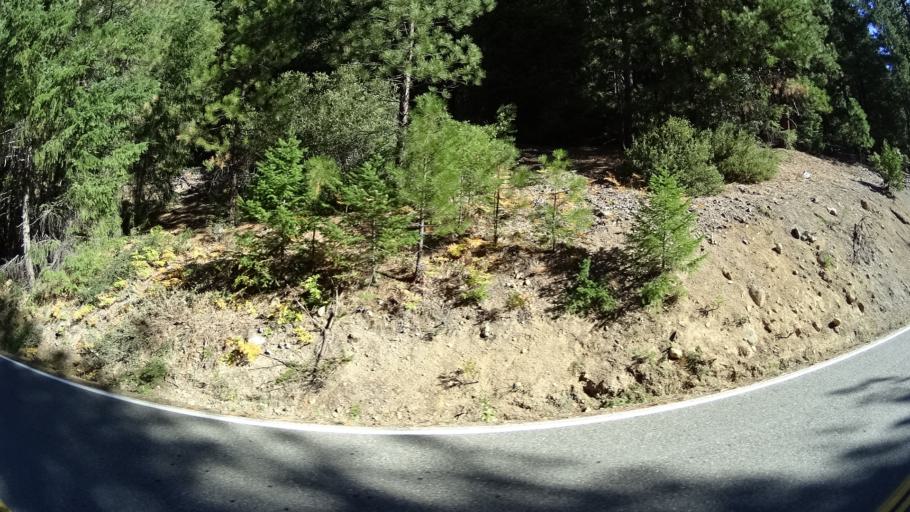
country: US
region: California
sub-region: Trinity County
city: Weaverville
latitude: 41.2298
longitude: -122.9596
